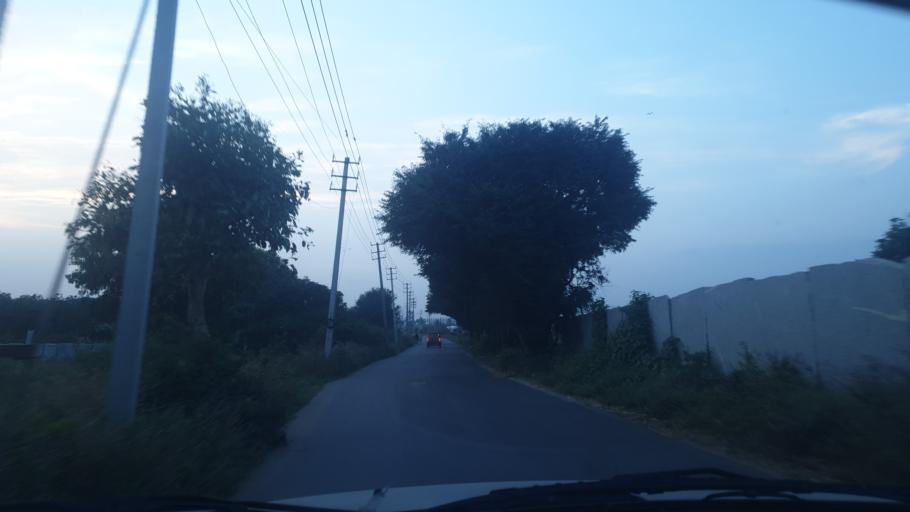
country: IN
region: Karnataka
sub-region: Bangalore Rural
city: Hoskote
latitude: 13.0776
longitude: 77.6962
